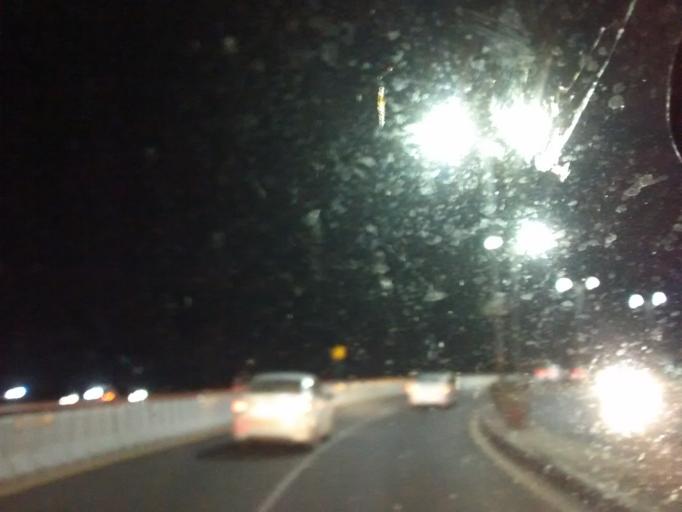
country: IN
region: Telangana
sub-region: Hyderabad
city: Hyderabad
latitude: 17.3264
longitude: 78.4258
